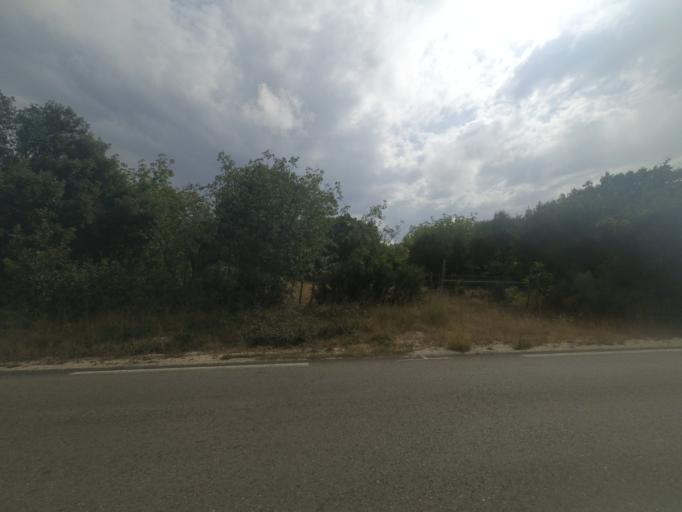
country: FR
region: Languedoc-Roussillon
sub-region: Departement de l'Herault
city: Les Matelles
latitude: 43.7400
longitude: 3.7811
